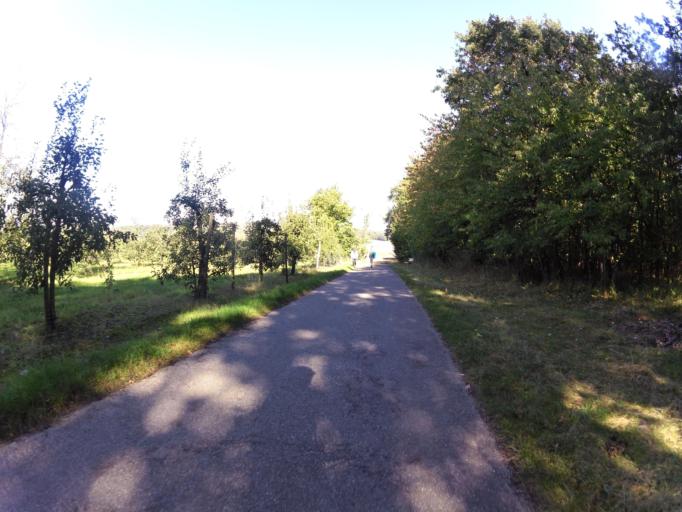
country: DE
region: Bavaria
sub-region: Regierungsbezirk Unterfranken
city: Sommerhausen
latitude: 49.6942
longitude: 10.0458
